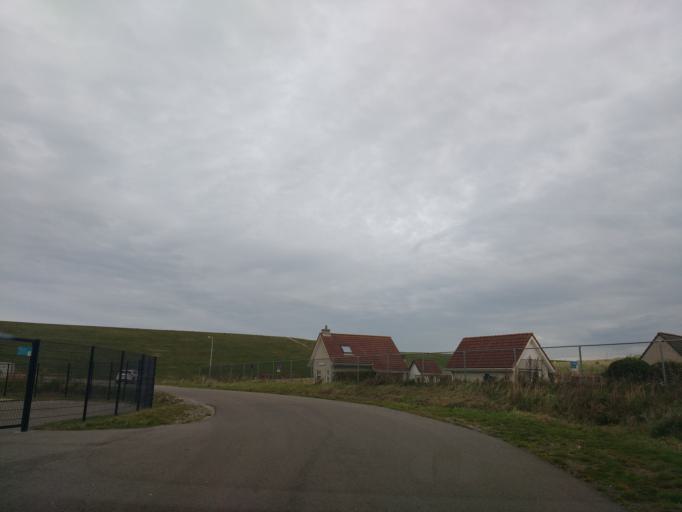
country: NL
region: Zeeland
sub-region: Gemeente Vlissingen
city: Vlissingen
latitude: 51.4044
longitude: 3.5051
